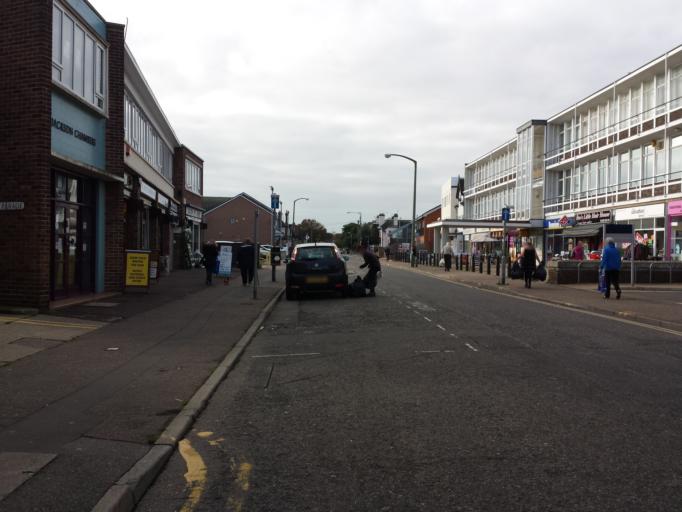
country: GB
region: England
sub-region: Essex
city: Clacton-on-Sea
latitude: 51.7897
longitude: 1.1510
